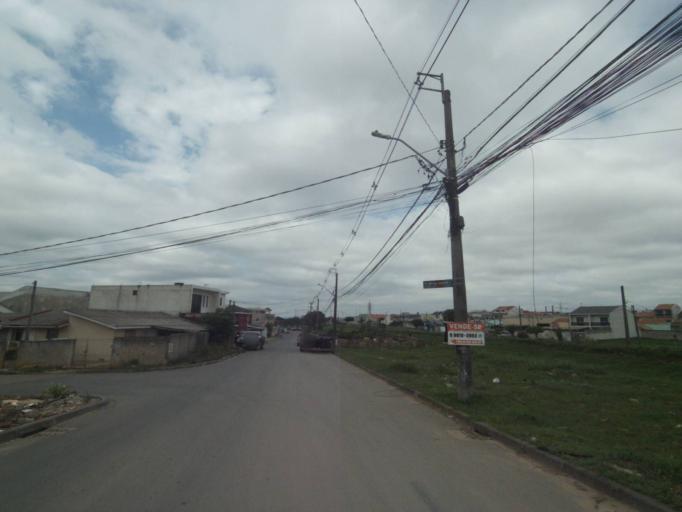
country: BR
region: Parana
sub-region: Sao Jose Dos Pinhais
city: Sao Jose dos Pinhais
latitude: -25.5490
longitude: -49.2526
